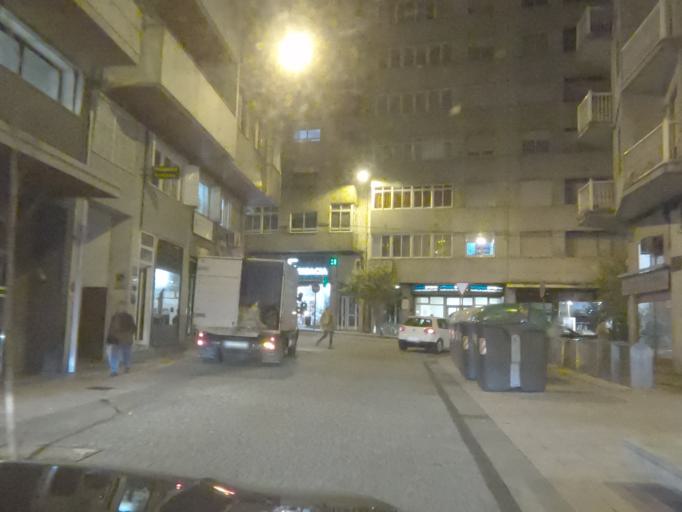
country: ES
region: Galicia
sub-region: Provincia de Ourense
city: Ourense
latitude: 42.3431
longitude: -7.8658
